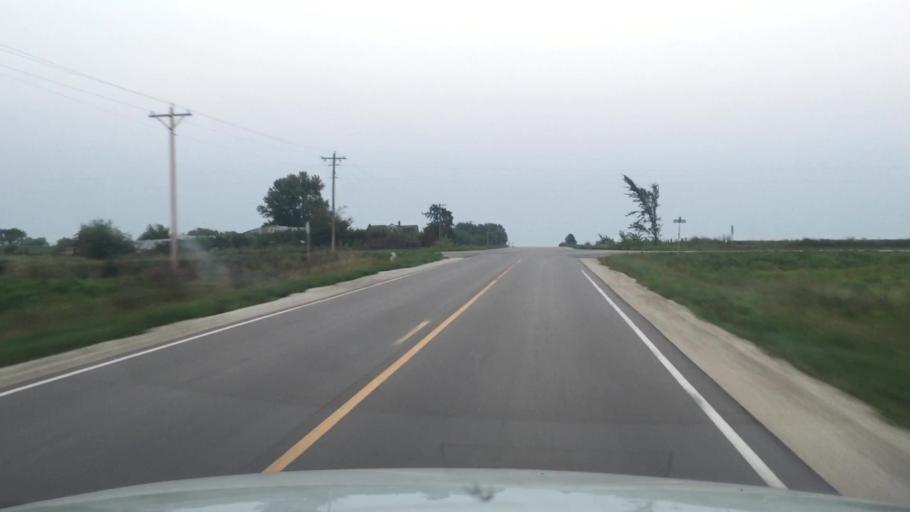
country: US
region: Iowa
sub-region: Warren County
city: Indianola
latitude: 41.1825
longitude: -93.4814
